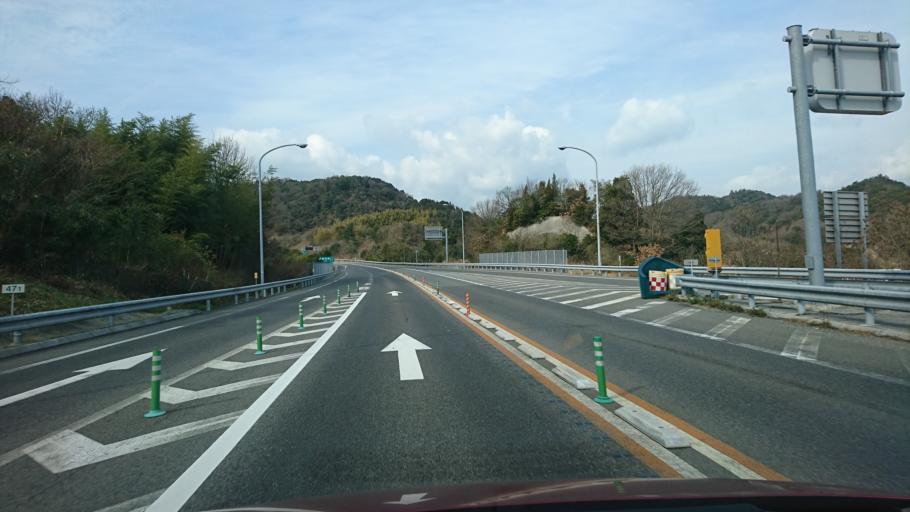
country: JP
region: Hiroshima
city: Innoshima
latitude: 34.1299
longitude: 133.0318
